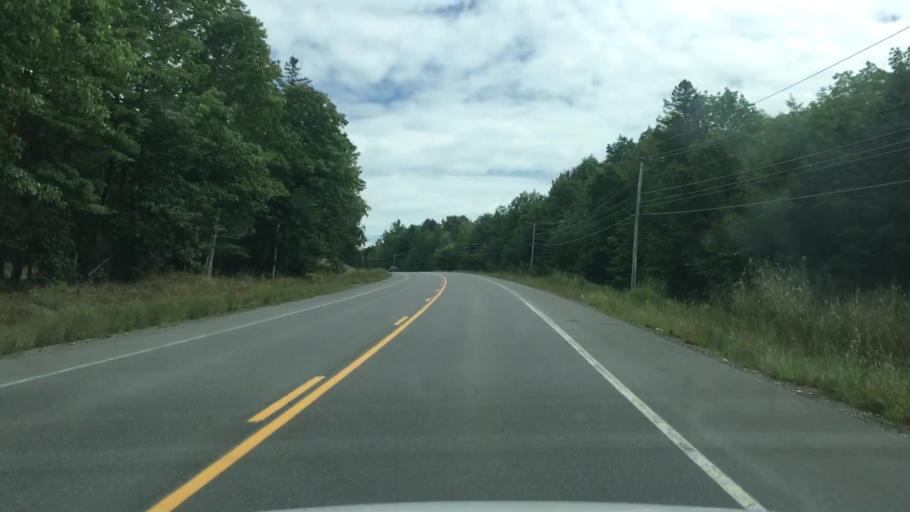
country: US
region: Maine
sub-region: Piscataquis County
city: Milo
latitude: 45.2423
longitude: -69.0221
